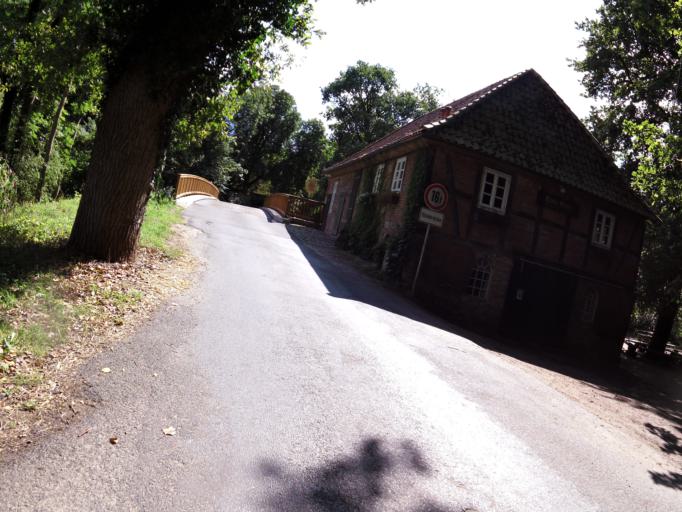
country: DE
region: Lower Saxony
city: Seedorf
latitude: 53.3343
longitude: 9.1994
